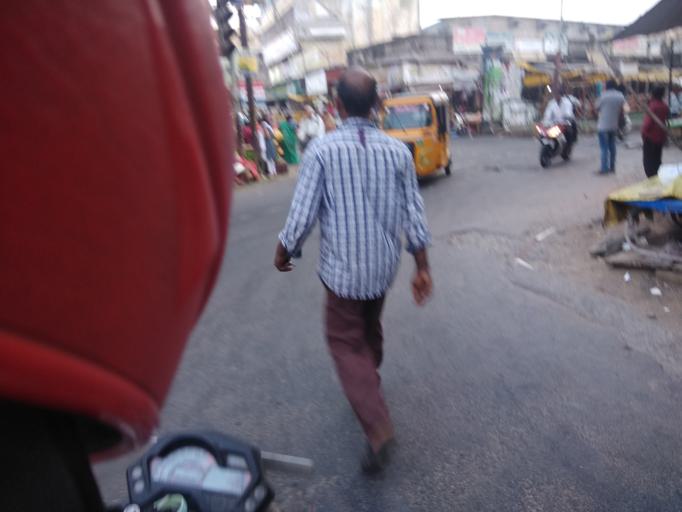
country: IN
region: Tamil Nadu
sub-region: Kancheepuram
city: Alandur
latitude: 13.0220
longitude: 80.2243
